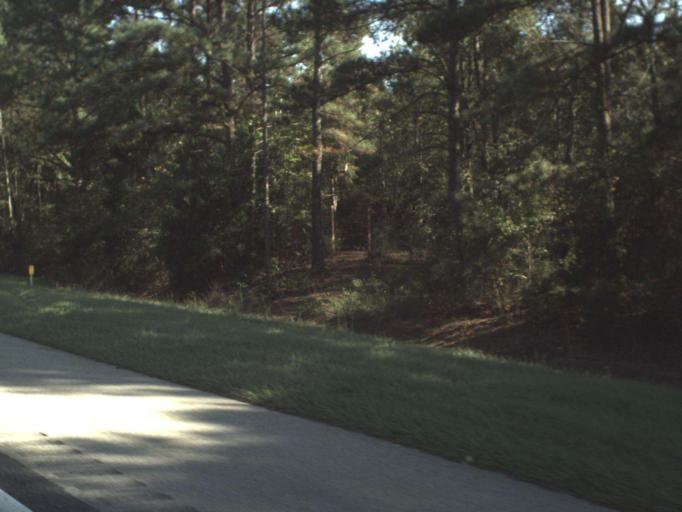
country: US
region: Florida
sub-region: Washington County
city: Chipley
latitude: 30.7446
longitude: -85.4809
